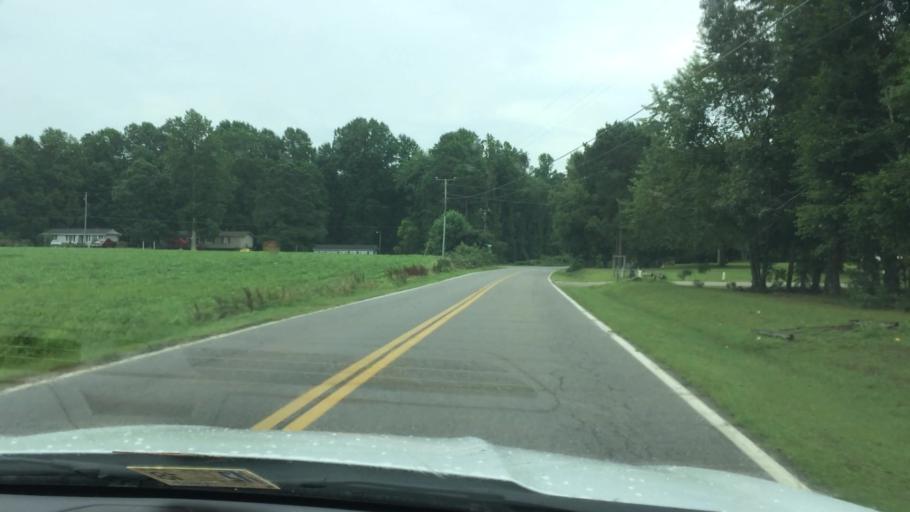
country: US
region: Virginia
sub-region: King William County
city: West Point
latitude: 37.5298
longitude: -76.7457
